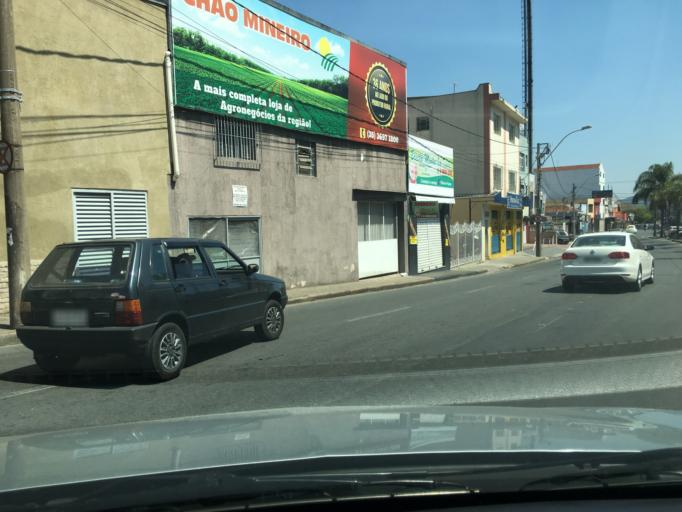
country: BR
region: Minas Gerais
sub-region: Pocos De Caldas
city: Pocos de Caldas
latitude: -21.7859
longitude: -46.5624
